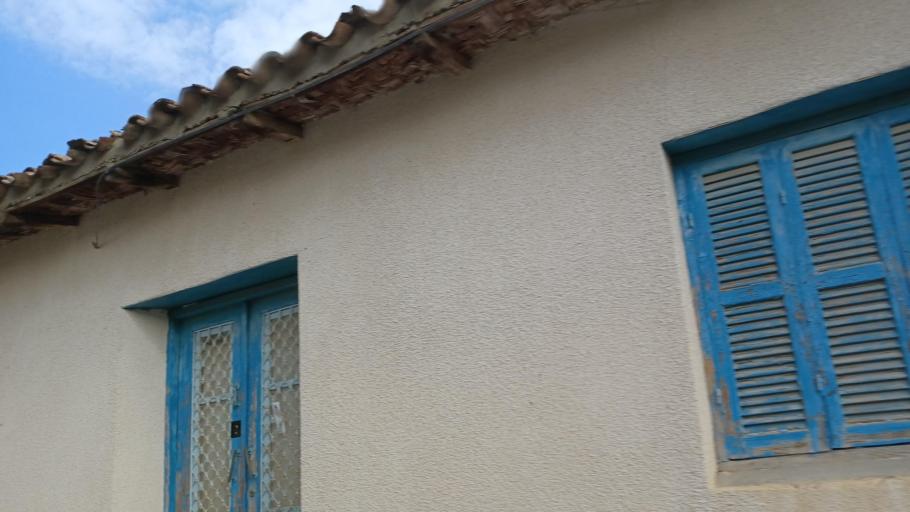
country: CY
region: Lefkosia
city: Klirou
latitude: 35.0426
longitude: 33.1240
